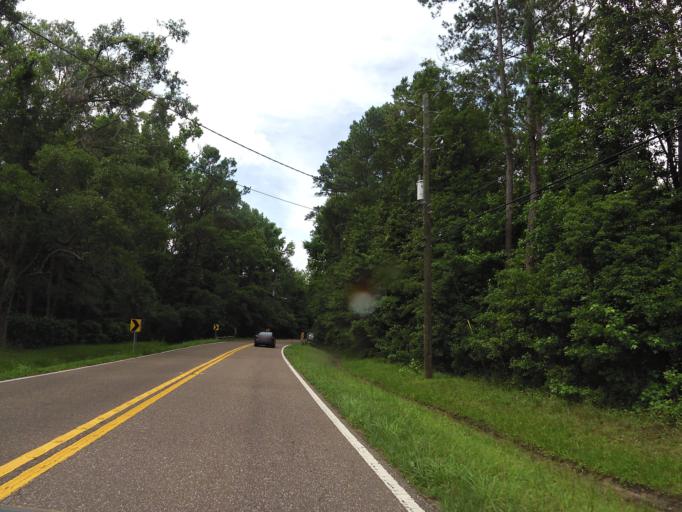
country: US
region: Florida
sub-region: Nassau County
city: Nassau Village-Ratliff
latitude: 30.5357
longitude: -81.7267
